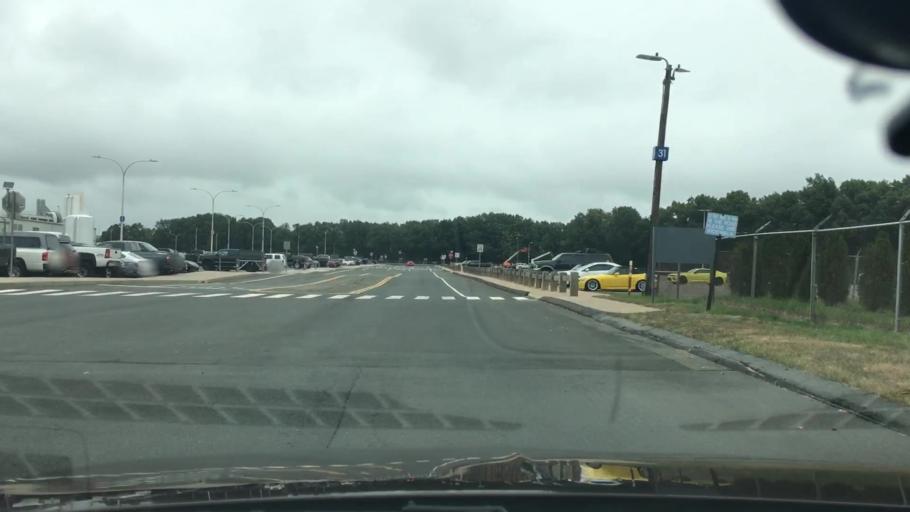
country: US
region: Connecticut
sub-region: Hartford County
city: Windsor Locks
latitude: 41.9226
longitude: -72.6847
